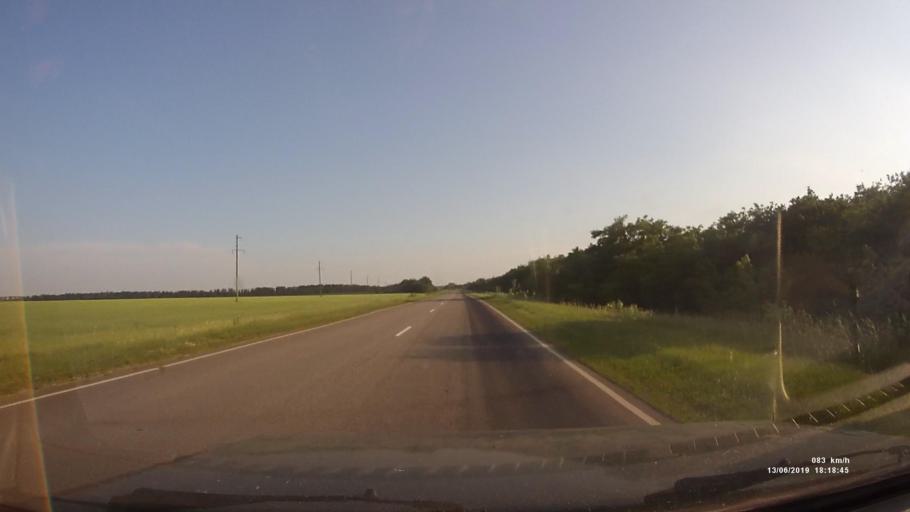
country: RU
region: Rostov
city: Kazanskaya
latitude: 49.9047
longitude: 41.3109
